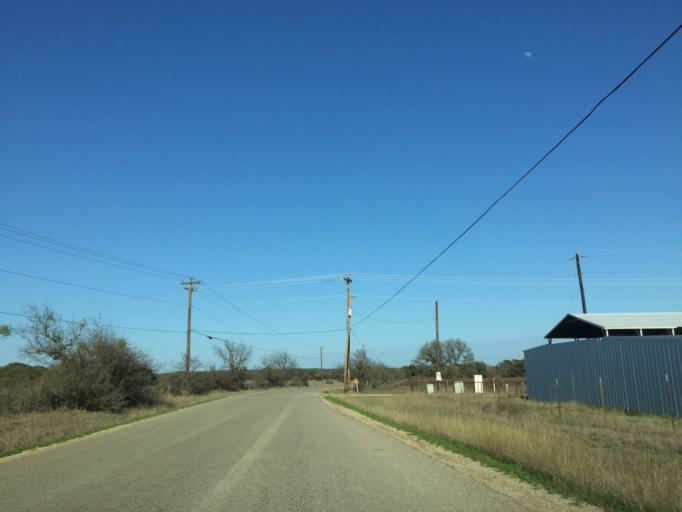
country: US
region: Texas
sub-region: Williamson County
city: Florence
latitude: 30.7728
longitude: -97.8163
